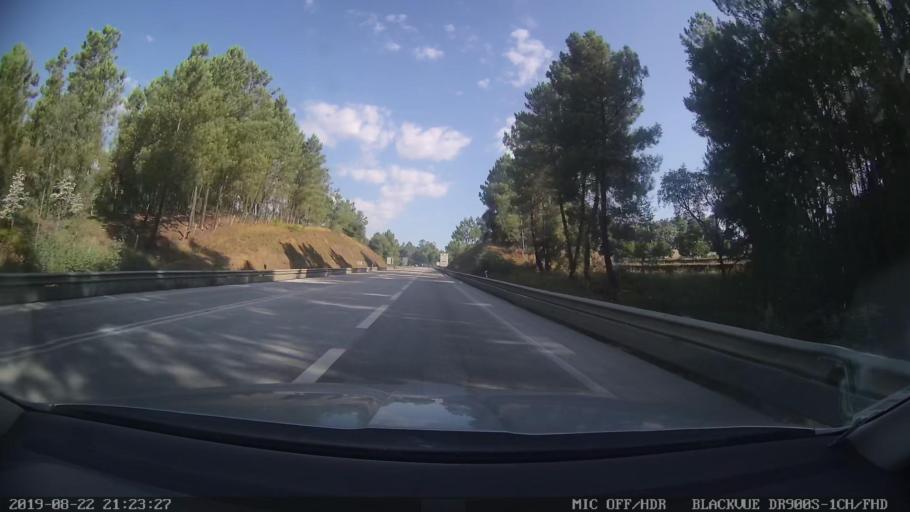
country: PT
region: Castelo Branco
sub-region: Serta
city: Serta
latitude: 39.8310
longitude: -8.1094
